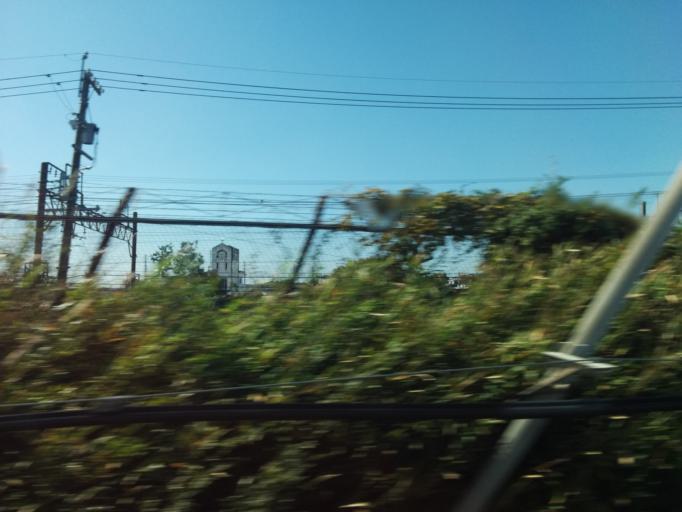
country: JP
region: Aichi
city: Obu
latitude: 35.0595
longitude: 136.9464
